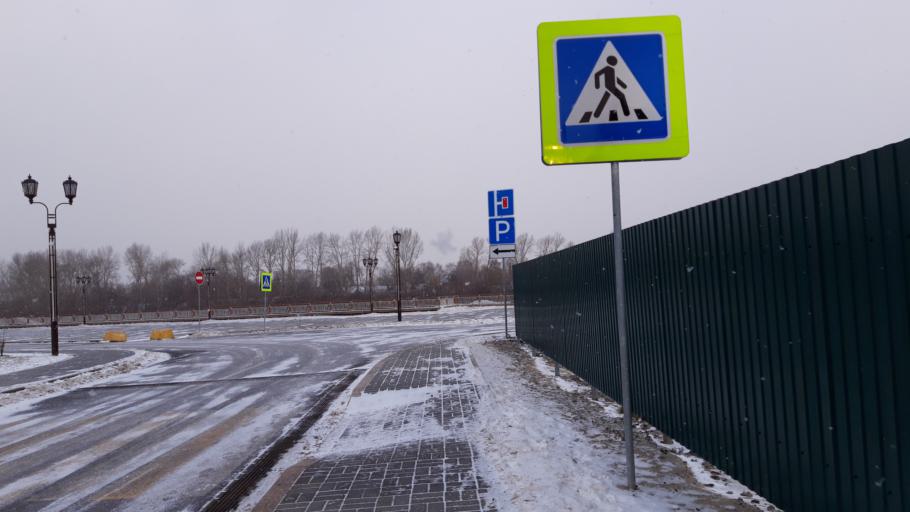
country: RU
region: Tjumen
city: Tyumen
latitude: 57.1618
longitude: 65.5498
